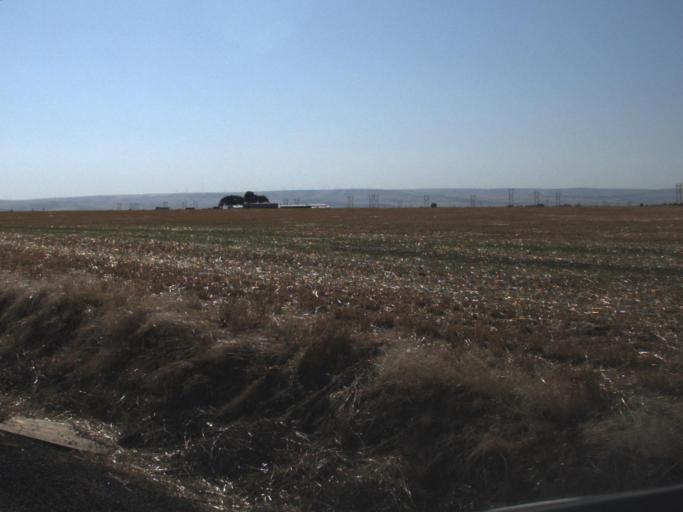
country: US
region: Washington
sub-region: Walla Walla County
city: Walla Walla
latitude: 46.0882
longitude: -118.3674
